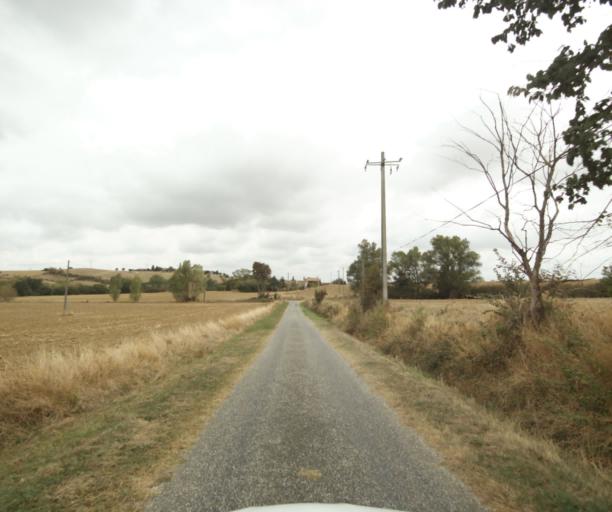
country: FR
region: Midi-Pyrenees
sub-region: Departement de la Haute-Garonne
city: Villefranche-de-Lauragais
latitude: 43.4123
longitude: 1.7268
